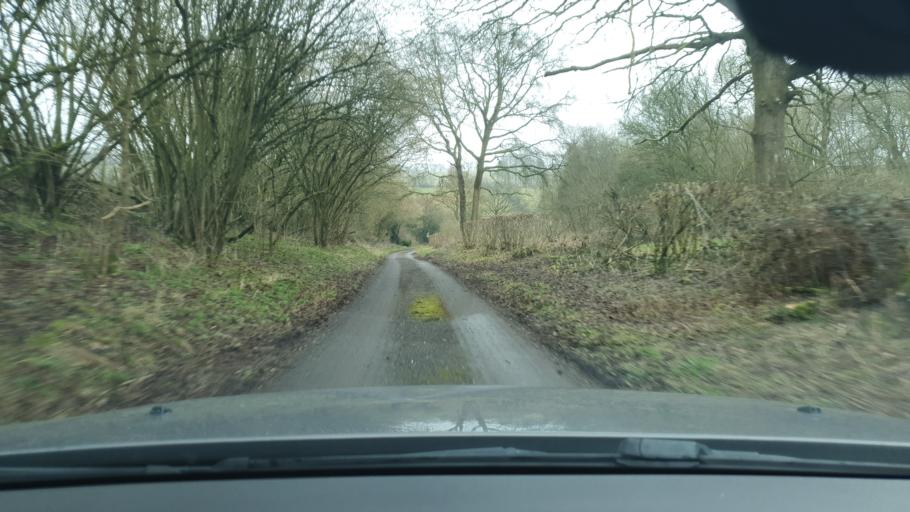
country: GB
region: England
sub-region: Wiltshire
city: Ramsbury
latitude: 51.4659
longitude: -1.5741
